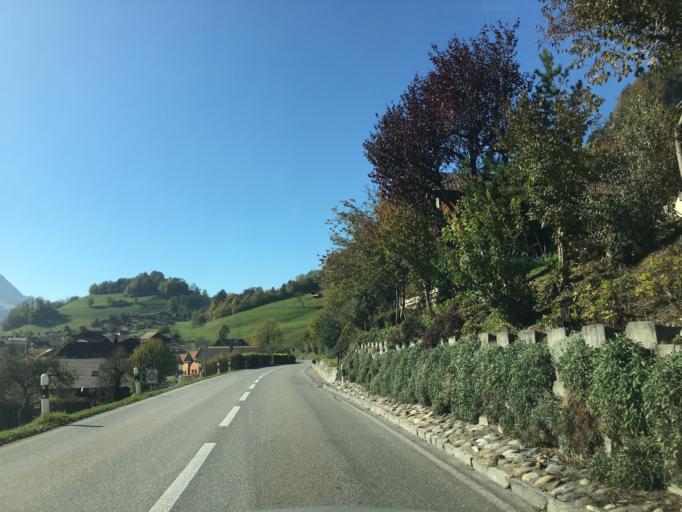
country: CH
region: Bern
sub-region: Frutigen-Niedersimmental District
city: Diemtigen
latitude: 46.6671
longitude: 7.5875
